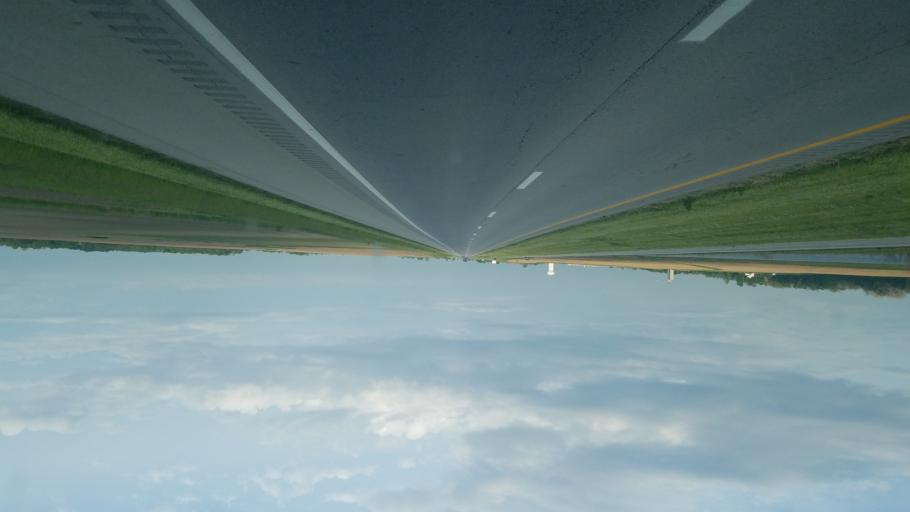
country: US
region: Ohio
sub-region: Clinton County
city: Wilmington
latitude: 39.4626
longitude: -83.7852
